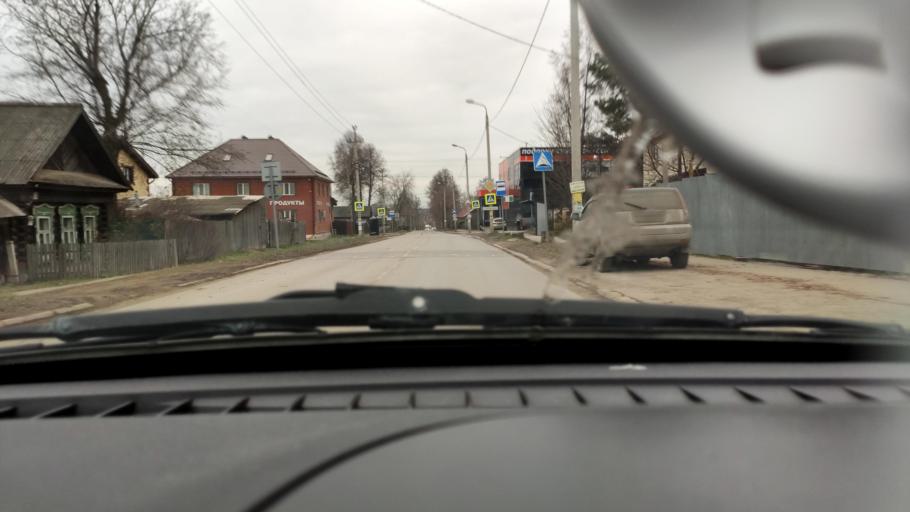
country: RU
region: Perm
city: Perm
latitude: 58.0263
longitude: 56.3325
